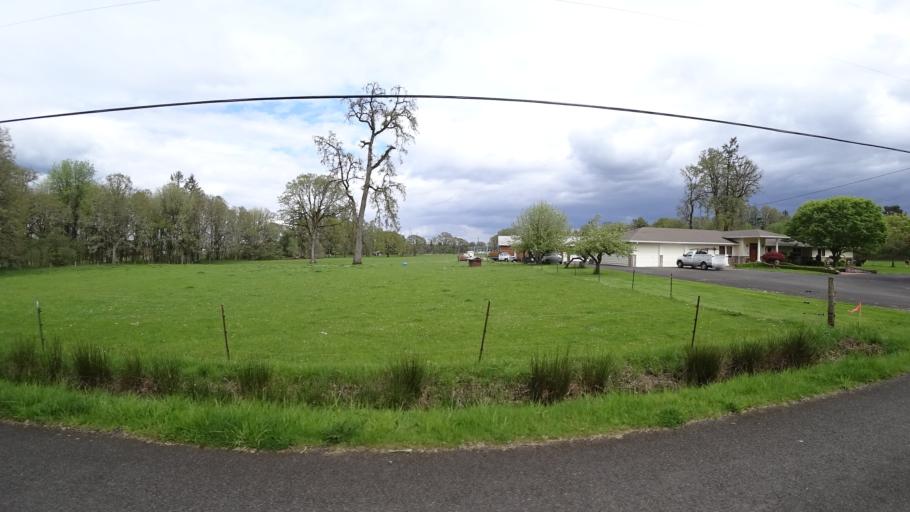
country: US
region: Oregon
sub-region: Washington County
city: Hillsboro
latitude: 45.5597
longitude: -122.9528
